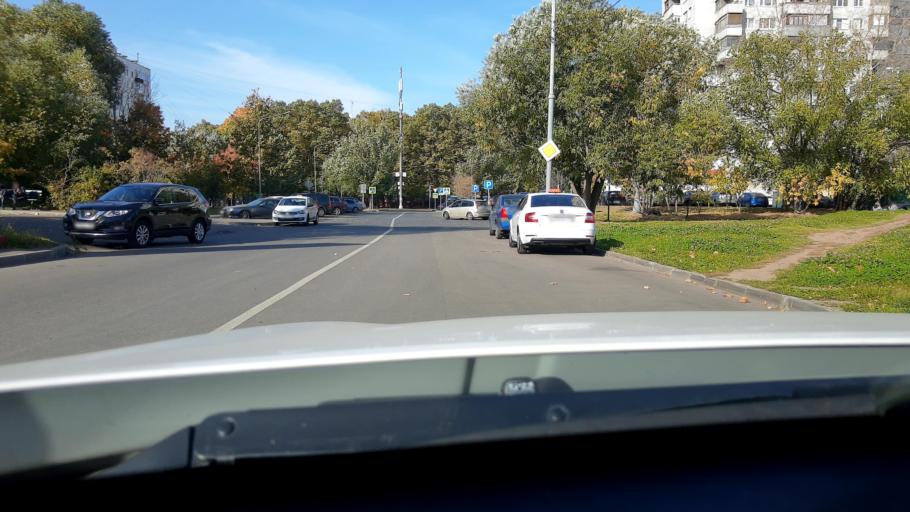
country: RU
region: Moscow
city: Likhobory
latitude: 55.8061
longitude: 37.5620
